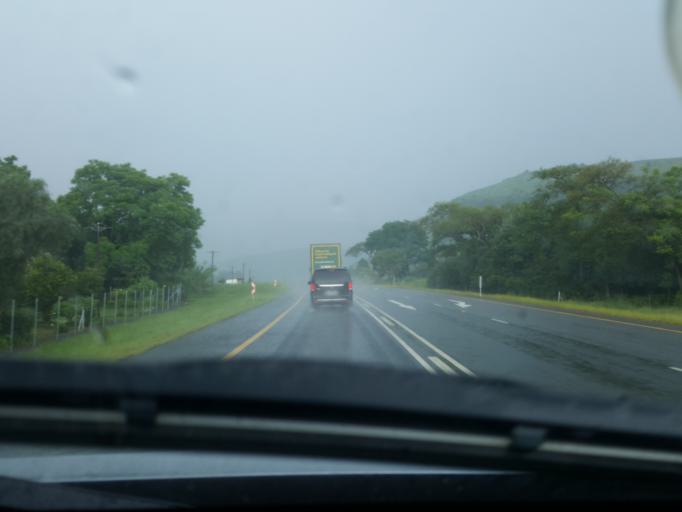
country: ZA
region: Mpumalanga
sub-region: Nkangala District Municipality
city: Belfast
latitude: -25.6062
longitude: 30.4363
